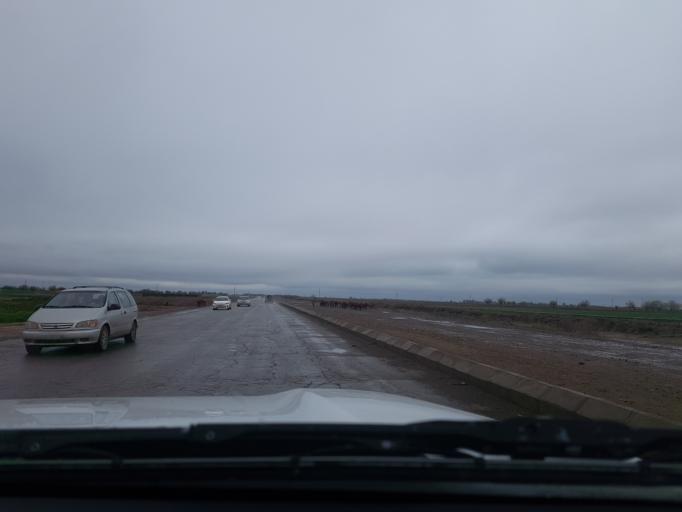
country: TM
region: Mary
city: Bayramaly
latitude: 37.5830
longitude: 62.1454
